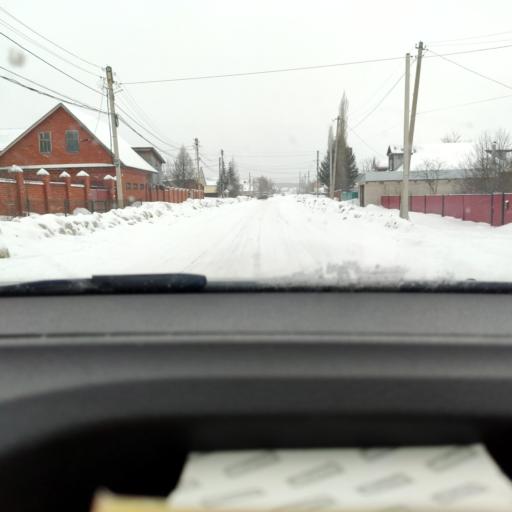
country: RU
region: Bashkortostan
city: Avdon
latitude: 54.4941
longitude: 55.8659
